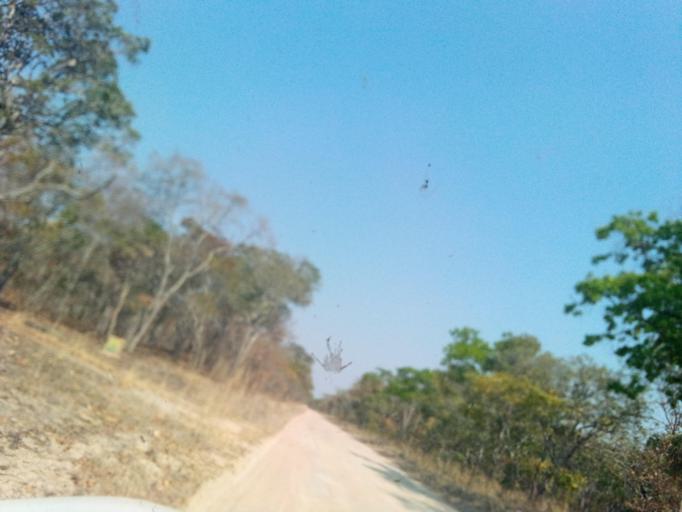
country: ZM
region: Northern
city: Mpika
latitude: -12.2259
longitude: 30.9013
